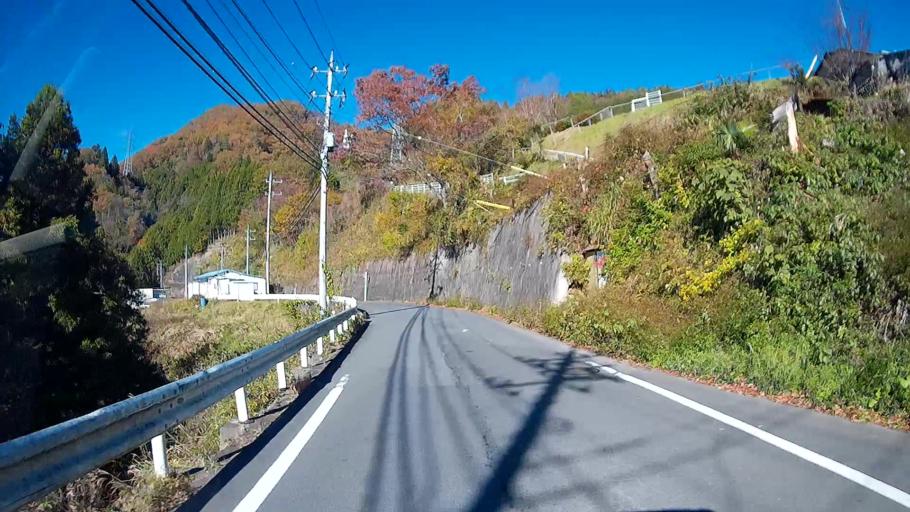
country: JP
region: Yamanashi
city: Uenohara
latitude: 35.5813
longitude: 139.1100
